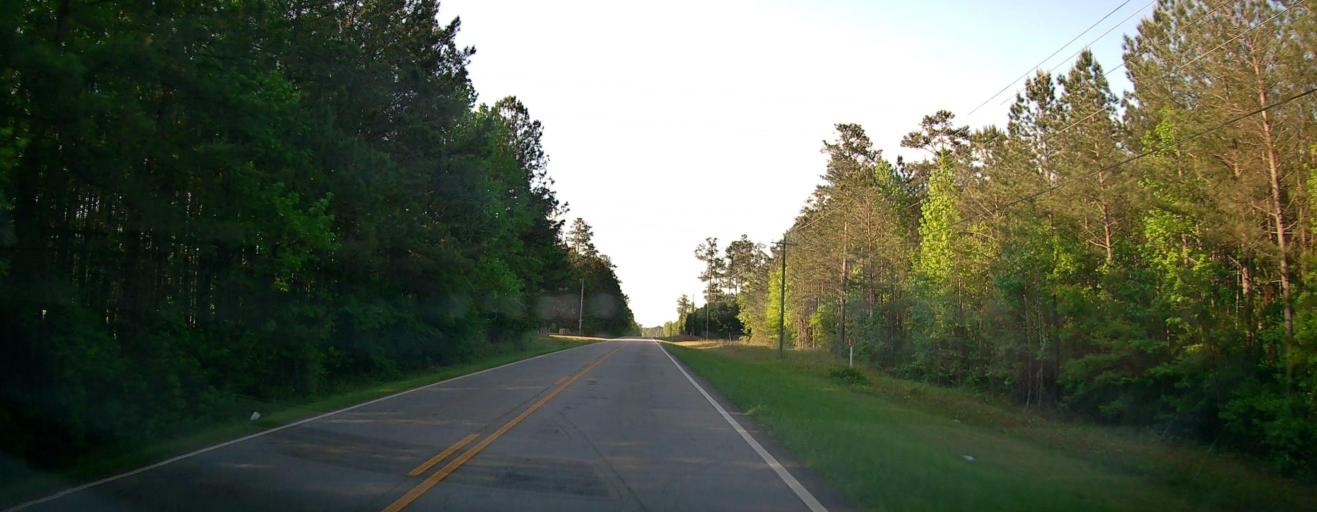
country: US
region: Georgia
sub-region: Putnam County
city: Eatonton
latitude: 33.2604
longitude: -83.3010
